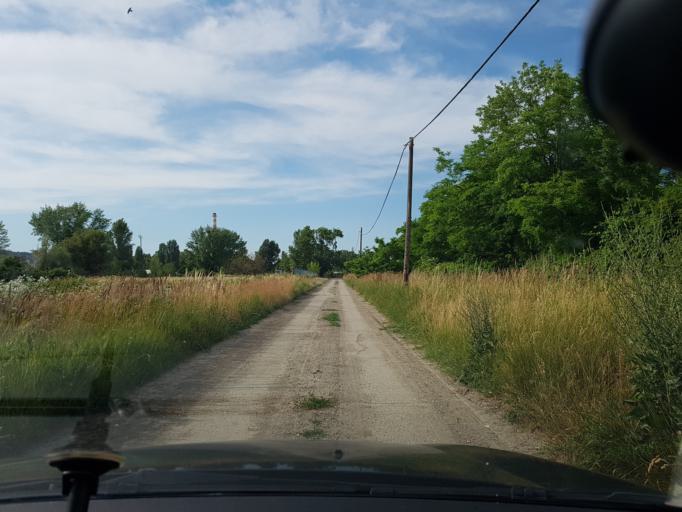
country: HU
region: Tolna
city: Szekszard
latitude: 46.3353
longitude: 18.7160
